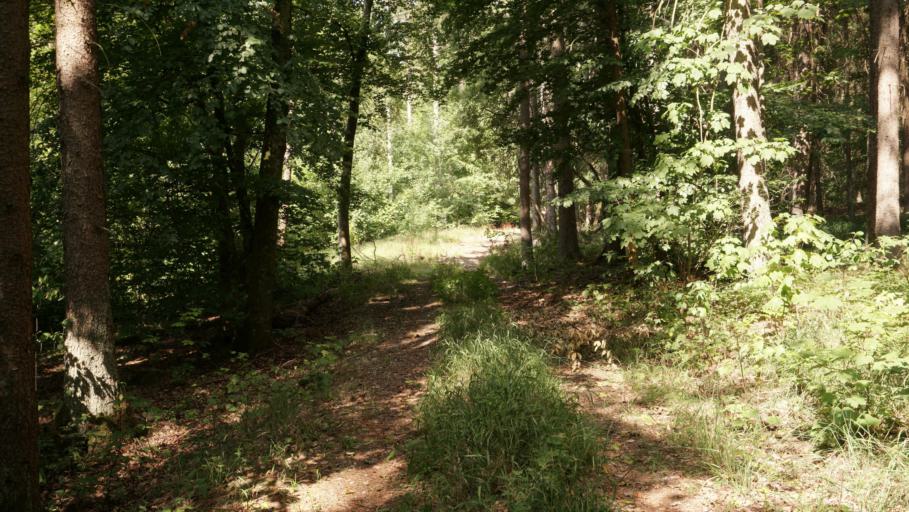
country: DE
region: Baden-Wuerttemberg
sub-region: Karlsruhe Region
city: Mosbach
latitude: 49.3834
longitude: 9.1565
